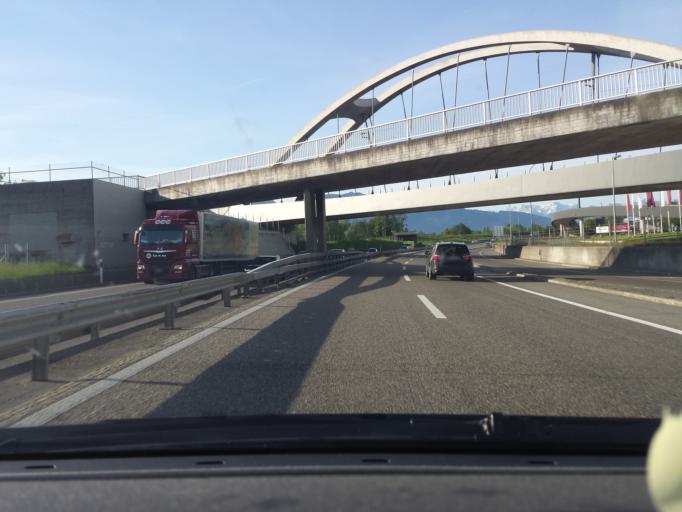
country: AT
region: Vorarlberg
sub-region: Politischer Bezirk Bregenz
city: Hochst
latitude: 47.4509
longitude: 9.6535
